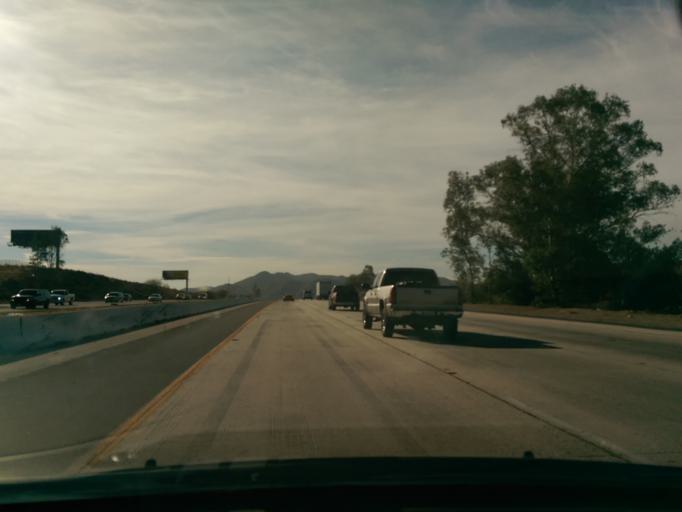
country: US
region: California
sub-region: Riverside County
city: Lake Elsinore
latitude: 33.6736
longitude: -117.3170
